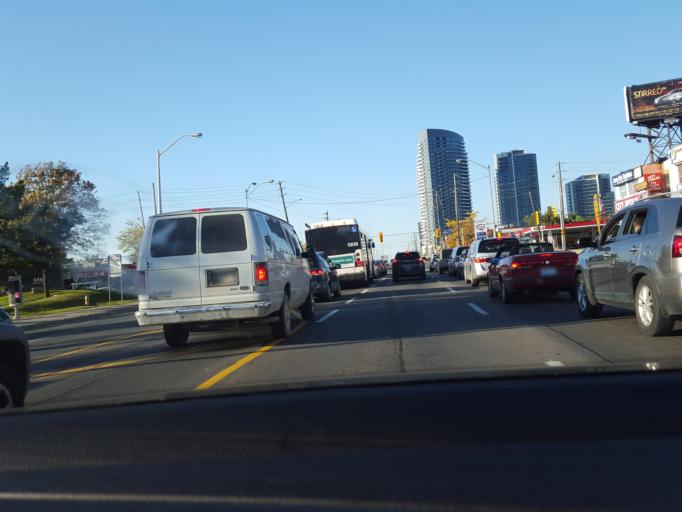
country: CA
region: Ontario
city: North York
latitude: 43.7972
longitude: -79.4198
